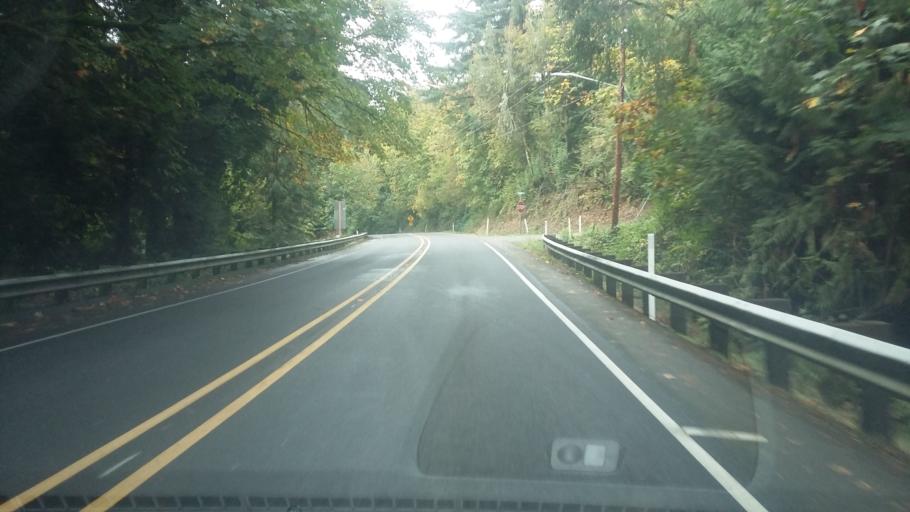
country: US
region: Washington
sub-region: Clark County
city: Ridgefield
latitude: 45.8160
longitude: -122.7182
